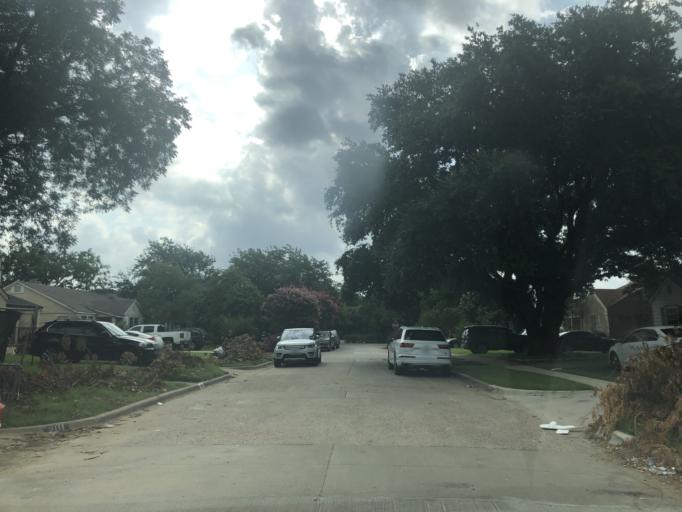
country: US
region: Texas
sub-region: Dallas County
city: University Park
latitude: 32.8522
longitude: -96.8238
